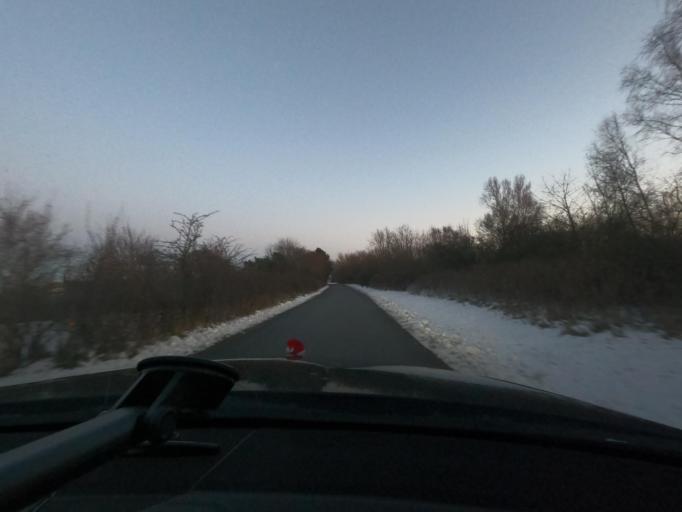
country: DK
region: South Denmark
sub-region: Sonderborg Kommune
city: Horuphav
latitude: 54.8657
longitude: 9.9072
